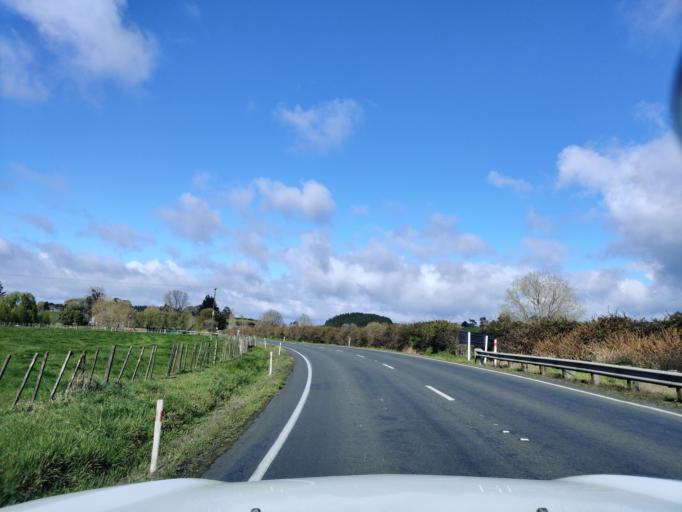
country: NZ
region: Waikato
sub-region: Otorohanga District
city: Otorohanga
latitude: -38.0507
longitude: 175.1653
